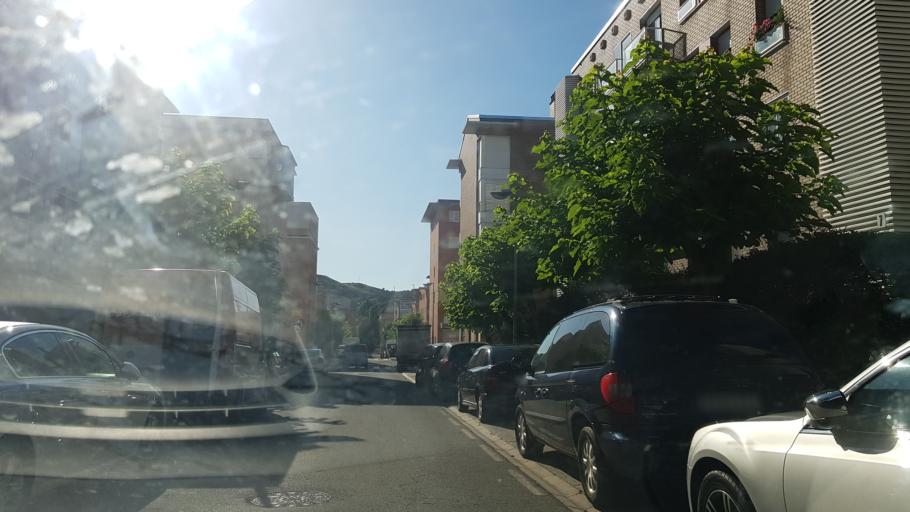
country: ES
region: Navarre
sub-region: Provincia de Navarra
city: Burlata
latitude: 42.8082
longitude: -1.6152
